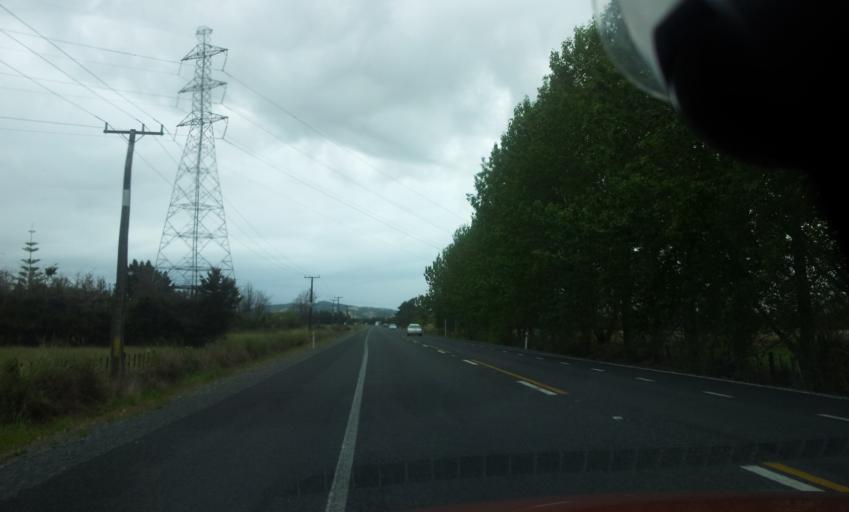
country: NZ
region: Northland
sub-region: Whangarei
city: Ruakaka
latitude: -35.9057
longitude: 174.4467
